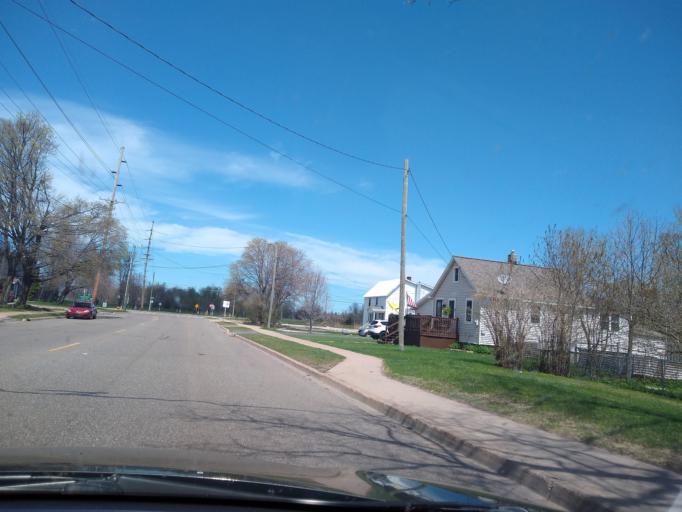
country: US
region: Michigan
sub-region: Marquette County
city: Marquette
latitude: 46.5701
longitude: -87.3961
